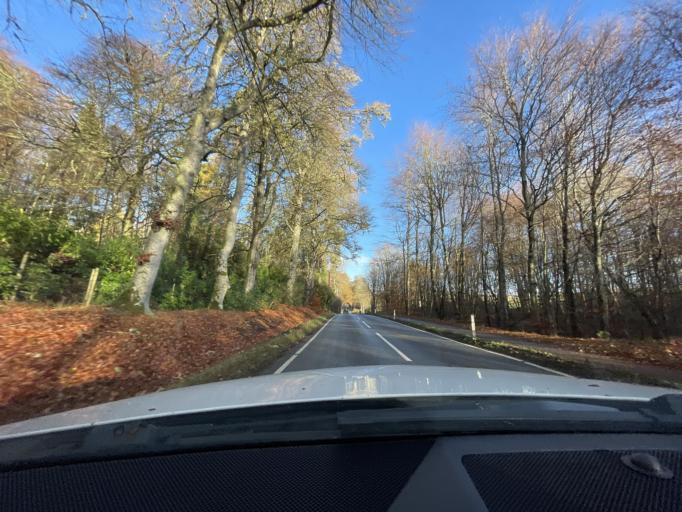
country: GB
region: Scotland
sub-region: Highland
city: Inverness
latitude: 57.4300
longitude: -4.2806
